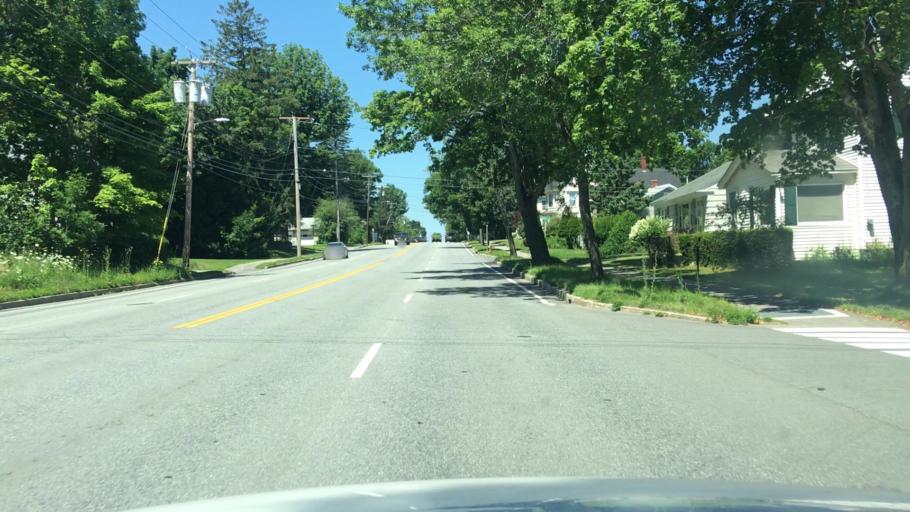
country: US
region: Maine
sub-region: Penobscot County
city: Bangor
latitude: 44.8098
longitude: -68.7951
